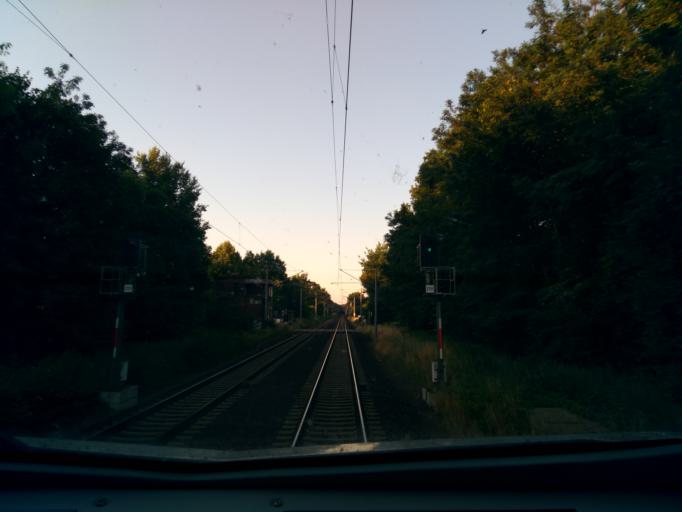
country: DE
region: Brandenburg
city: Konigs Wusterhausen
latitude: 52.2792
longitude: 13.6328
